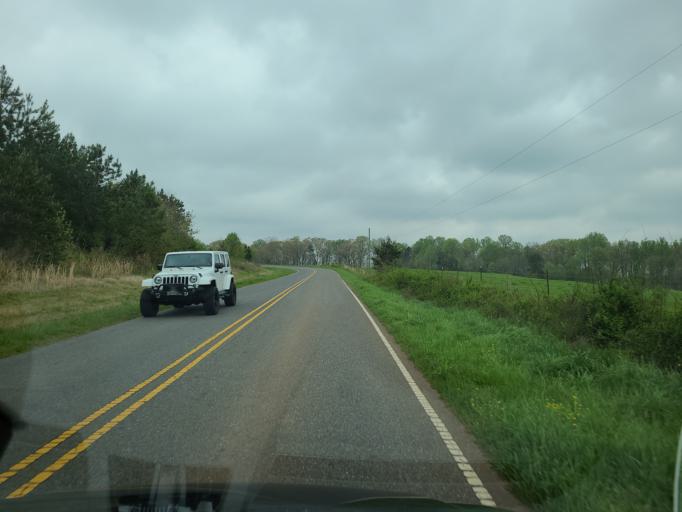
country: US
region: North Carolina
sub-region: Gaston County
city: Cherryville
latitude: 35.4272
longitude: -81.4625
